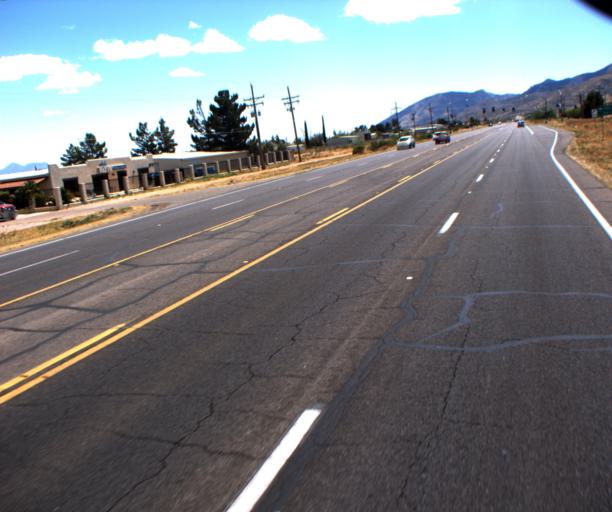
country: US
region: Arizona
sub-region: Cochise County
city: Sierra Vista Southeast
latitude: 31.4839
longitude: -110.2575
